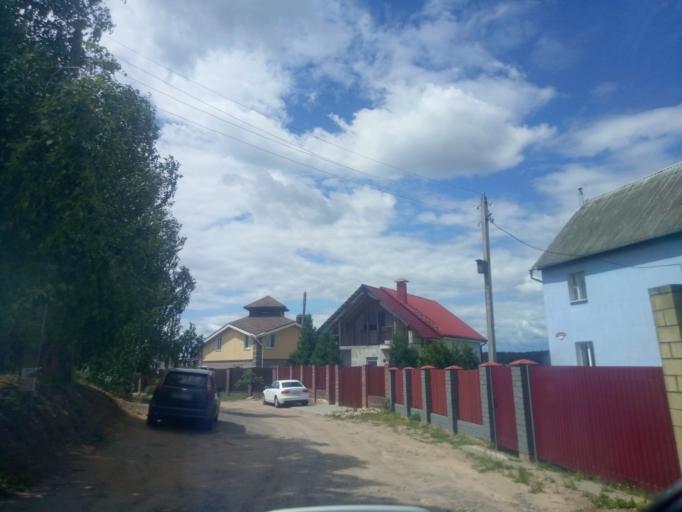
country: BY
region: Minsk
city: Zhdanovichy
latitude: 53.9373
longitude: 27.4083
